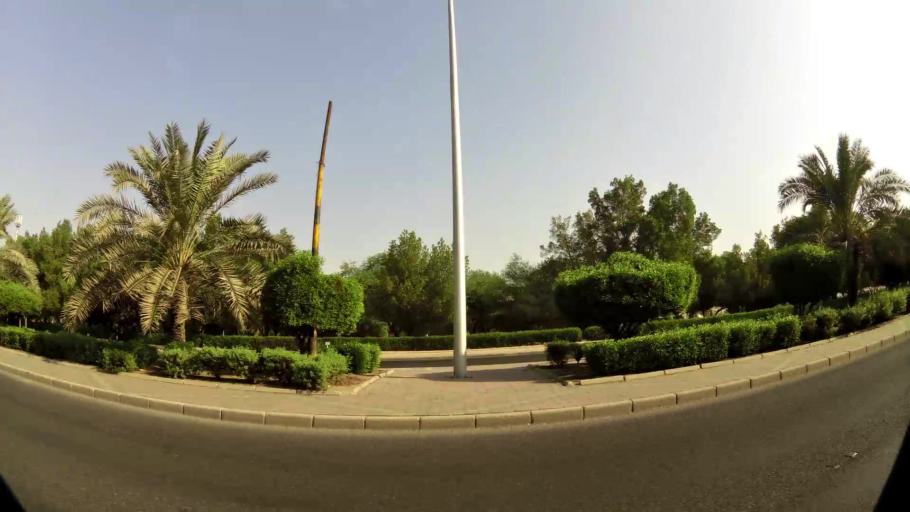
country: KW
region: Muhafazat Hawalli
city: Hawalli
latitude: 29.3490
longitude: 48.0154
